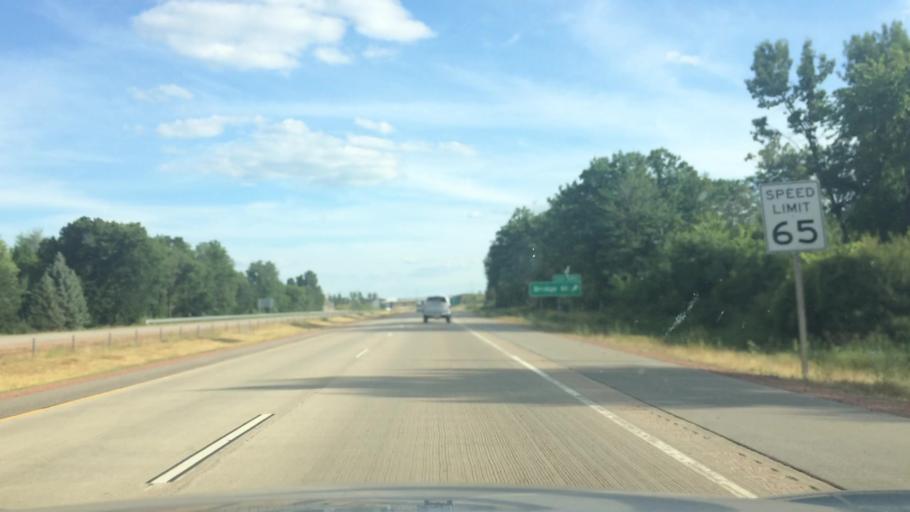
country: US
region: Wisconsin
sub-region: Marathon County
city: Wausau
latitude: 44.9765
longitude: -89.6572
